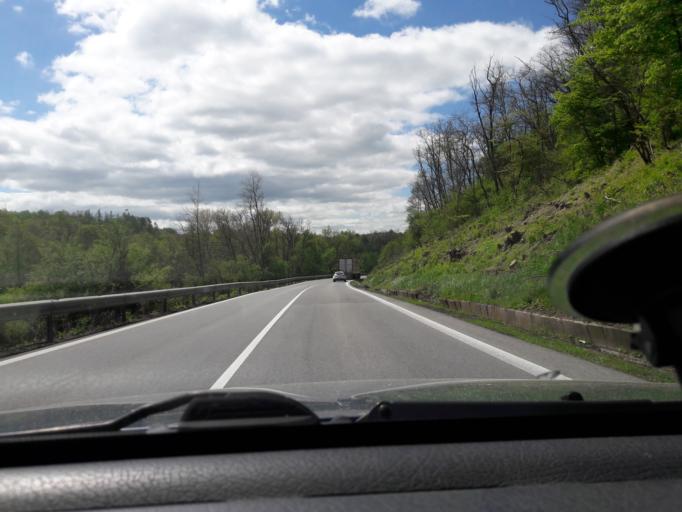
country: SK
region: Banskobystricky
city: Krupina
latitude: 48.3802
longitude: 19.0772
